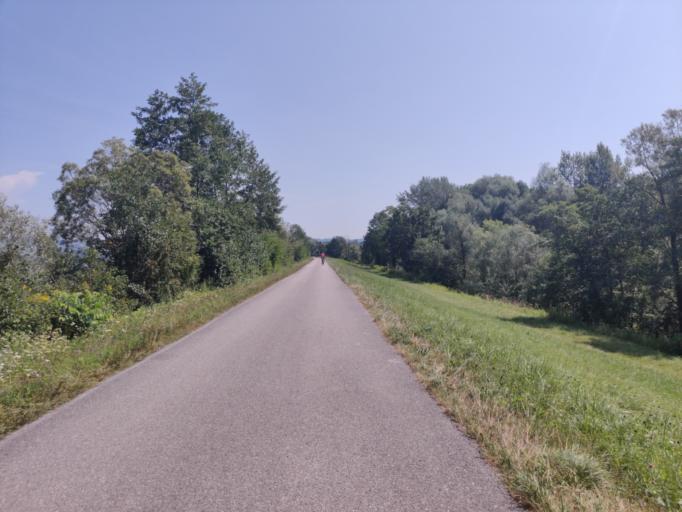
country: AT
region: Upper Austria
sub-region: Politischer Bezirk Urfahr-Umgebung
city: Goldworth
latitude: 48.3080
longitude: 14.1135
